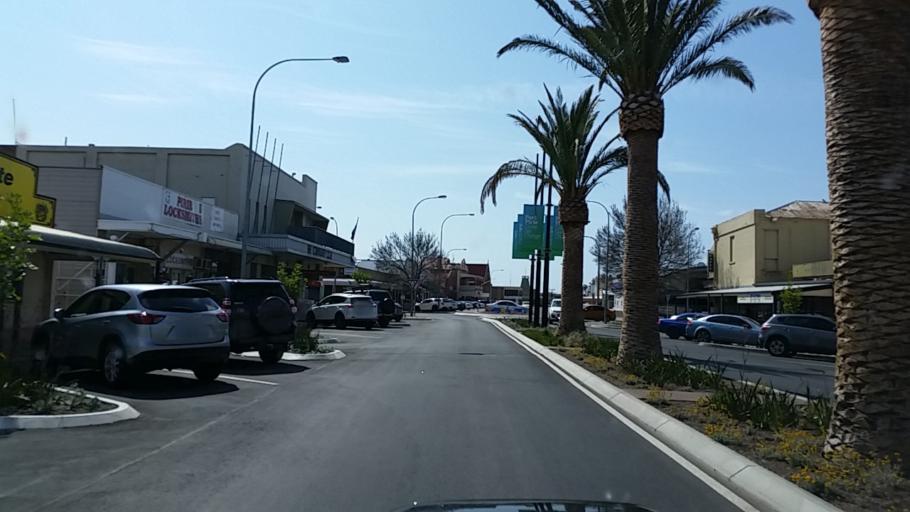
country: AU
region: South Australia
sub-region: Port Pirie City and Dists
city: Port Pirie
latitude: -33.1779
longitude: 138.0088
